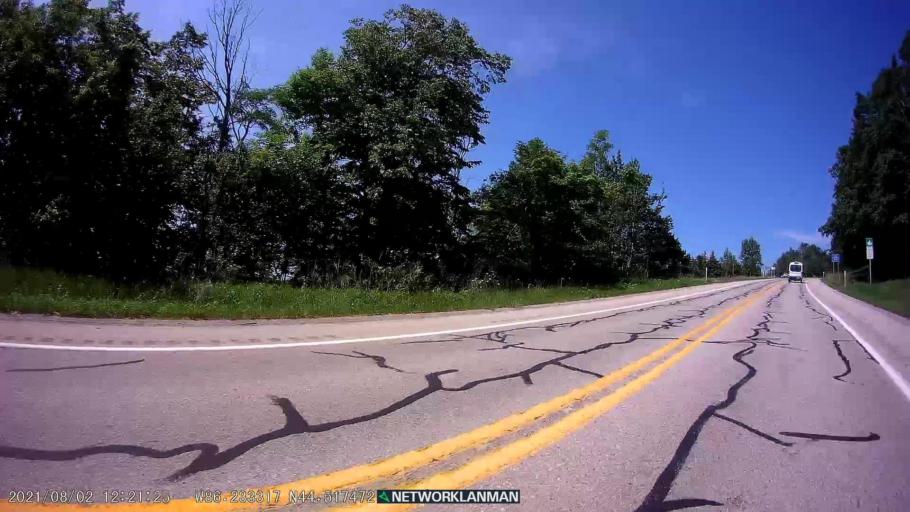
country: US
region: Michigan
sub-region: Benzie County
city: Frankfort
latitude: 44.5176
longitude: -86.2333
